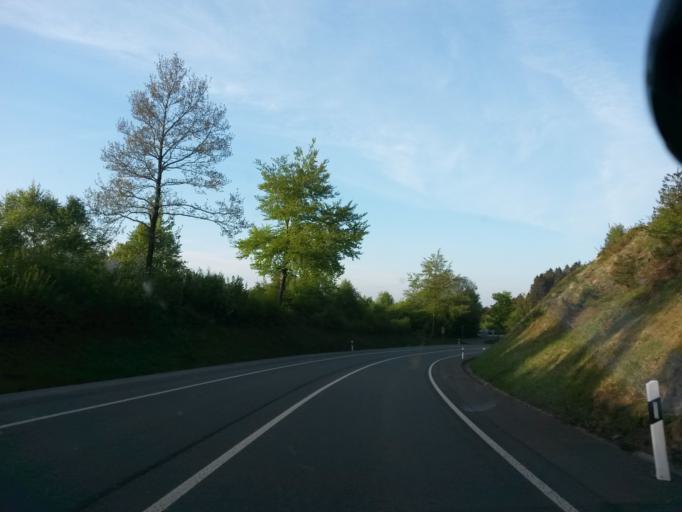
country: DE
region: North Rhine-Westphalia
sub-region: Regierungsbezirk Arnsberg
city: Herscheid
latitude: 51.1631
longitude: 7.7436
